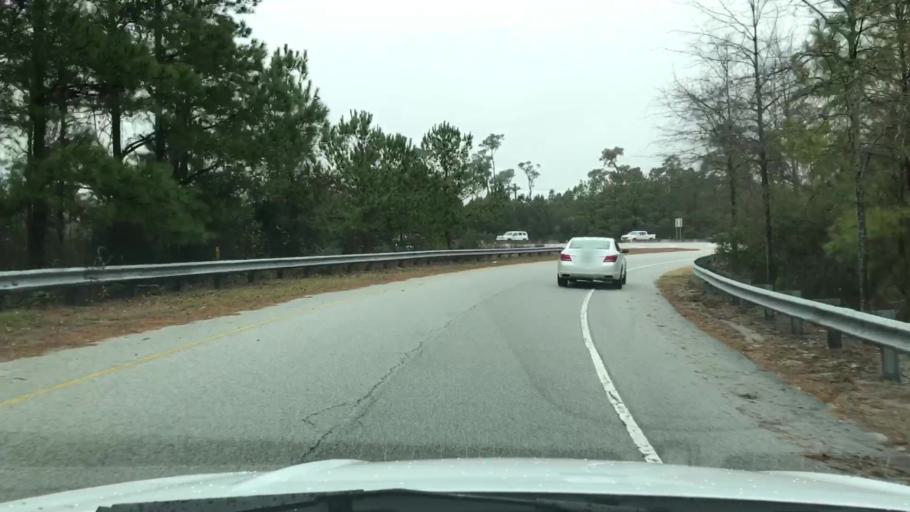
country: US
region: South Carolina
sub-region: Horry County
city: Myrtle Beach
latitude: 33.7406
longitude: -78.8501
